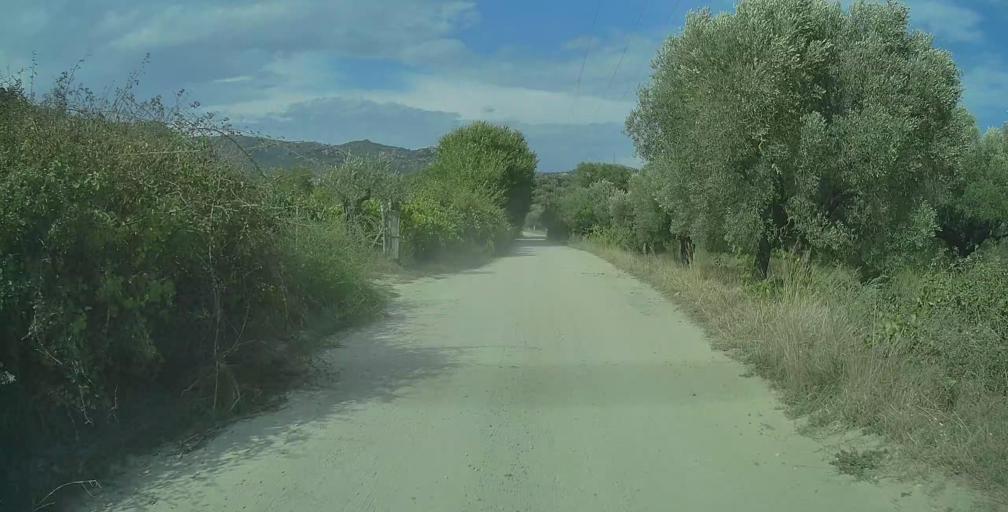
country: GR
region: Central Macedonia
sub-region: Nomos Chalkidikis
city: Sykia
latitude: 40.0309
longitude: 23.9438
